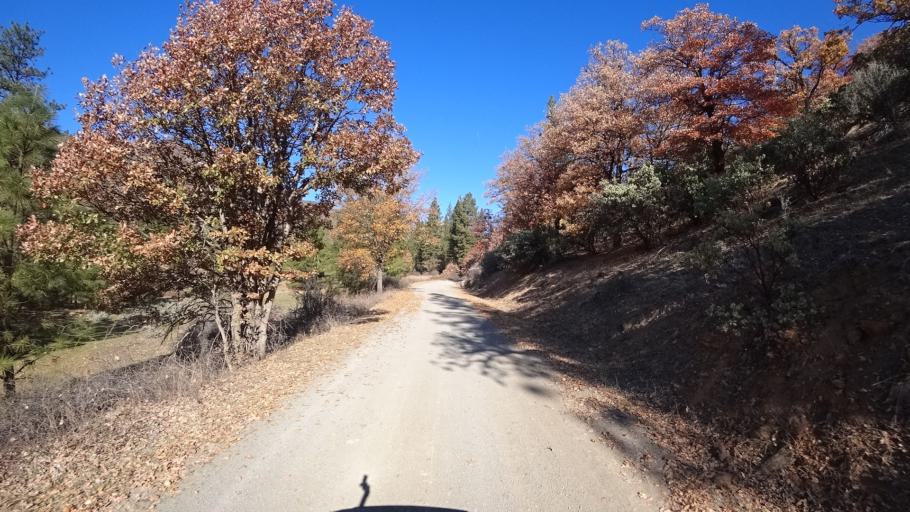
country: US
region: California
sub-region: Siskiyou County
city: Yreka
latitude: 41.8403
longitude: -122.8360
